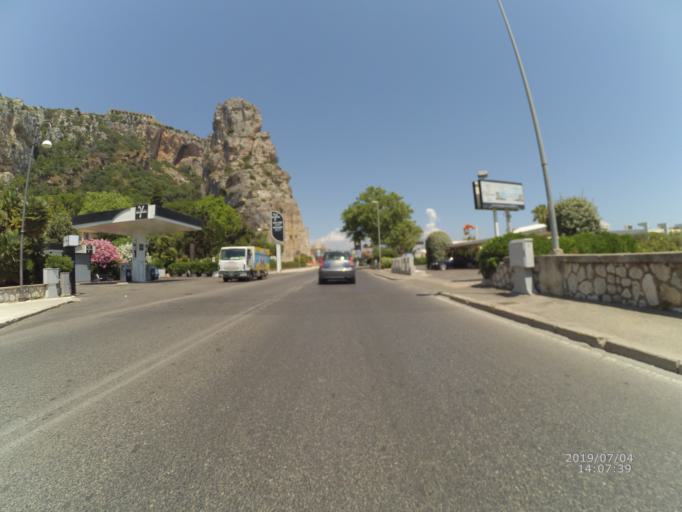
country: IT
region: Latium
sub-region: Provincia di Latina
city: Terracina
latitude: 41.2873
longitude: 13.2579
